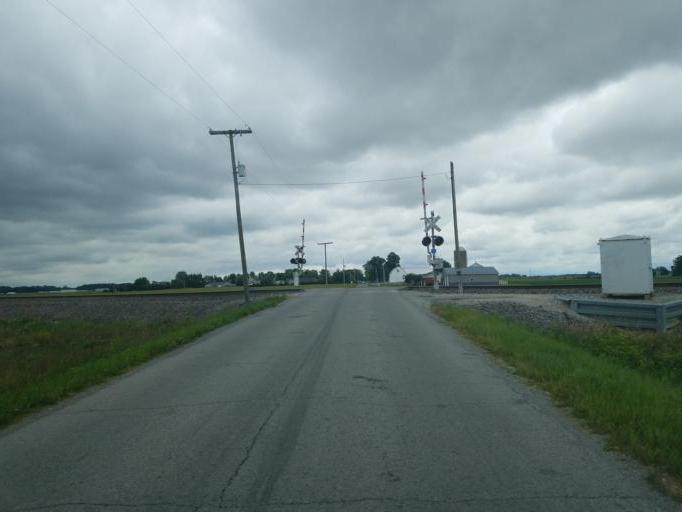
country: US
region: Ohio
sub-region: Crawford County
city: Bucyrus
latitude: 40.7757
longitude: -82.9880
